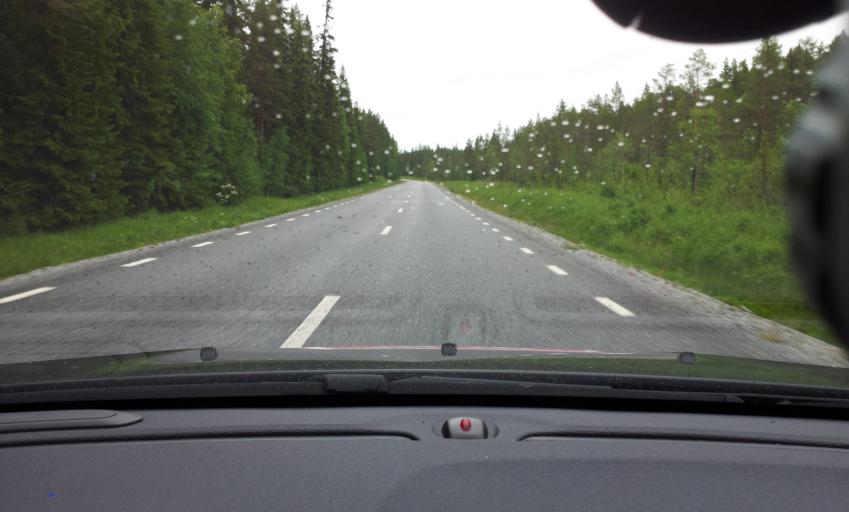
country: SE
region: Jaemtland
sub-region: OEstersunds Kommun
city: Lit
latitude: 63.6942
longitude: 14.6831
